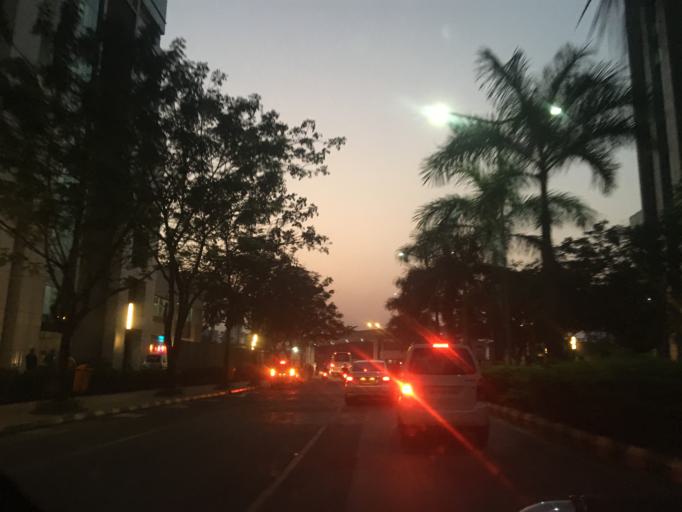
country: IN
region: Maharashtra
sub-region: Thane
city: Airoli
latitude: 19.1626
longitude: 73.0013
